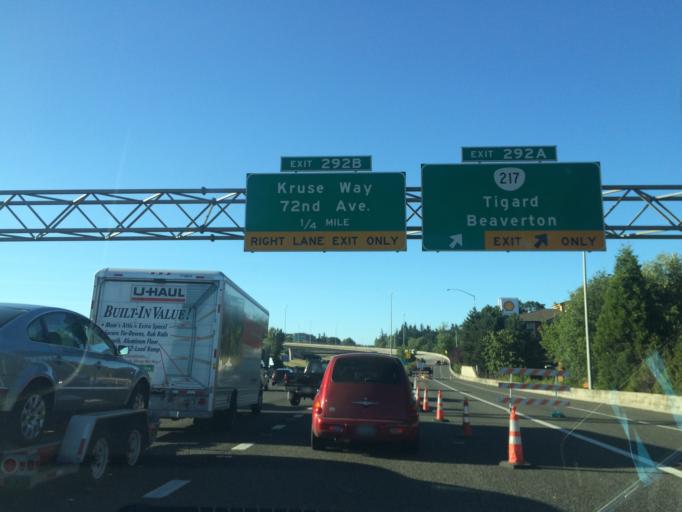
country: US
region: Oregon
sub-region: Washington County
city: Durham
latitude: 45.4168
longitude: -122.7438
